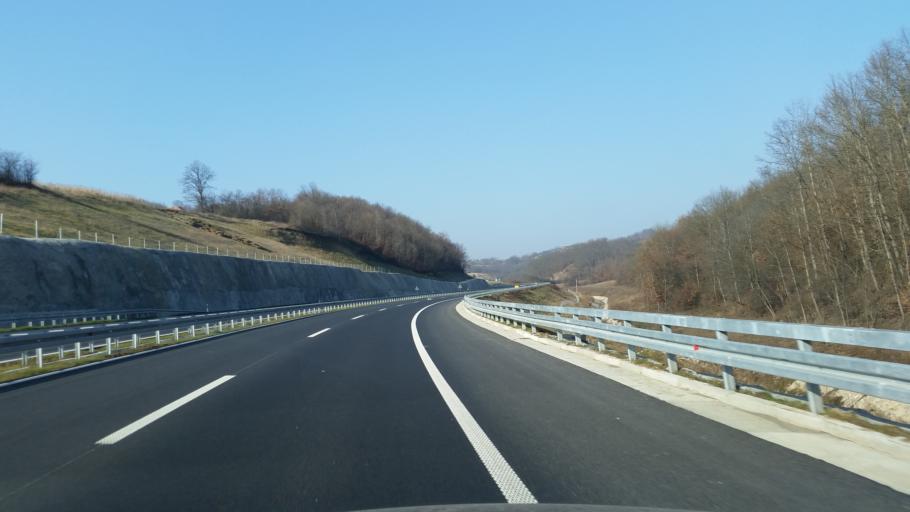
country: RS
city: Prislonica
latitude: 44.0037
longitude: 20.3931
